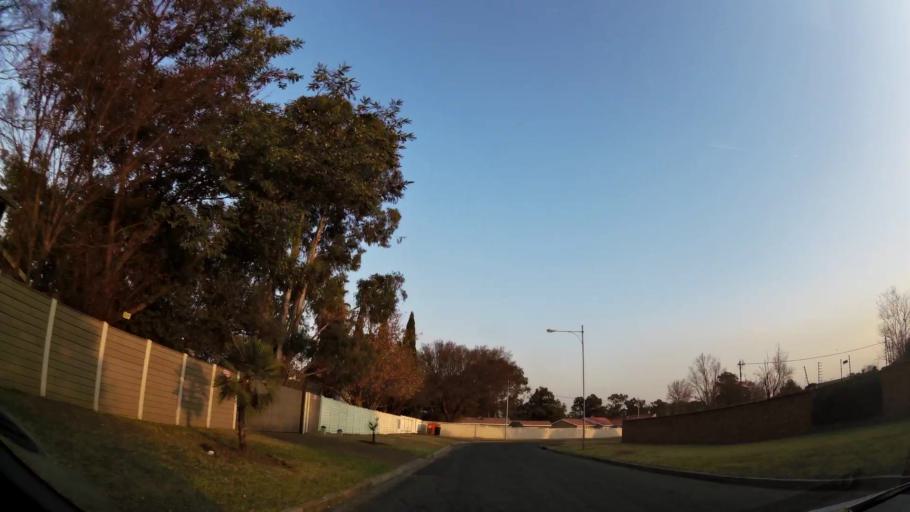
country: ZA
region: Gauteng
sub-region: Ekurhuleni Metropolitan Municipality
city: Springs
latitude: -26.3131
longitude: 28.4534
